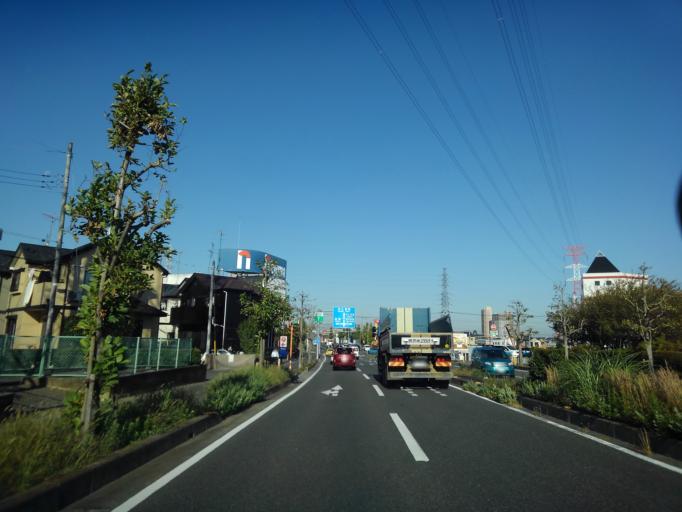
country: JP
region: Saitama
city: Tokorozawa
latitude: 35.7907
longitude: 139.4456
